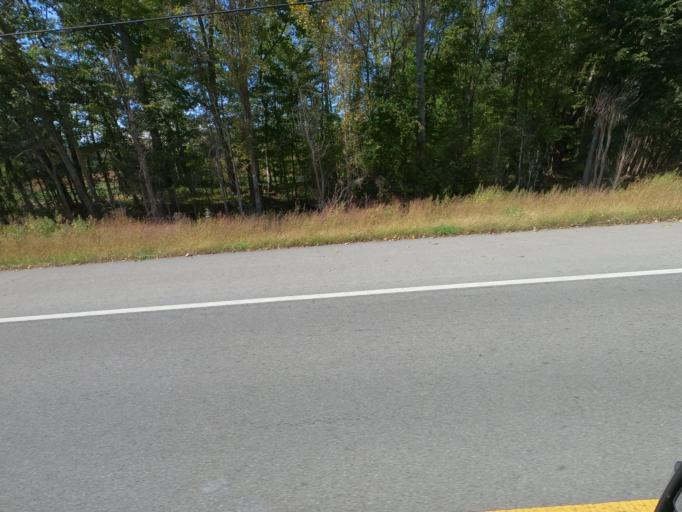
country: US
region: Tennessee
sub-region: Cheatham County
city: Pleasant View
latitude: 36.4480
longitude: -87.1007
